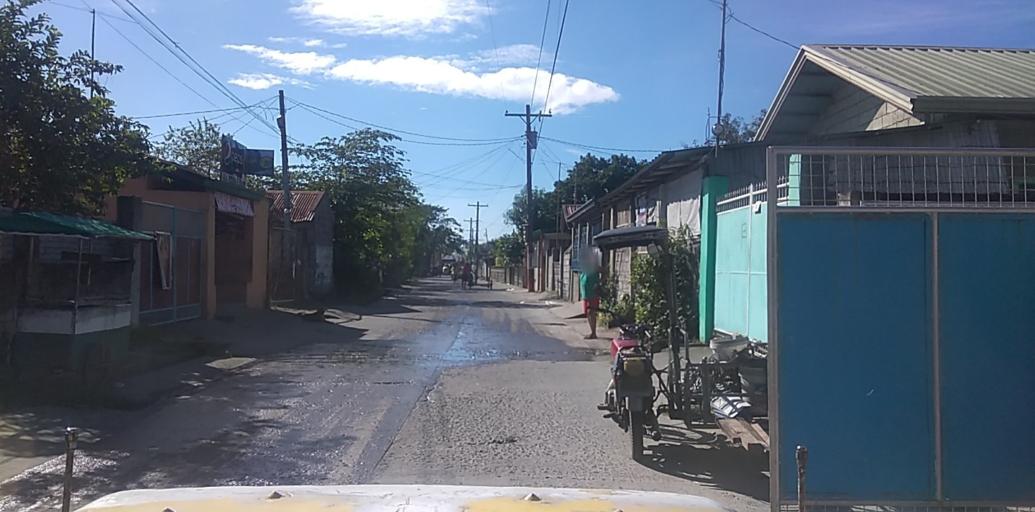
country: PH
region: Central Luzon
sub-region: Province of Pampanga
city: San Patricio
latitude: 15.0993
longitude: 120.7136
